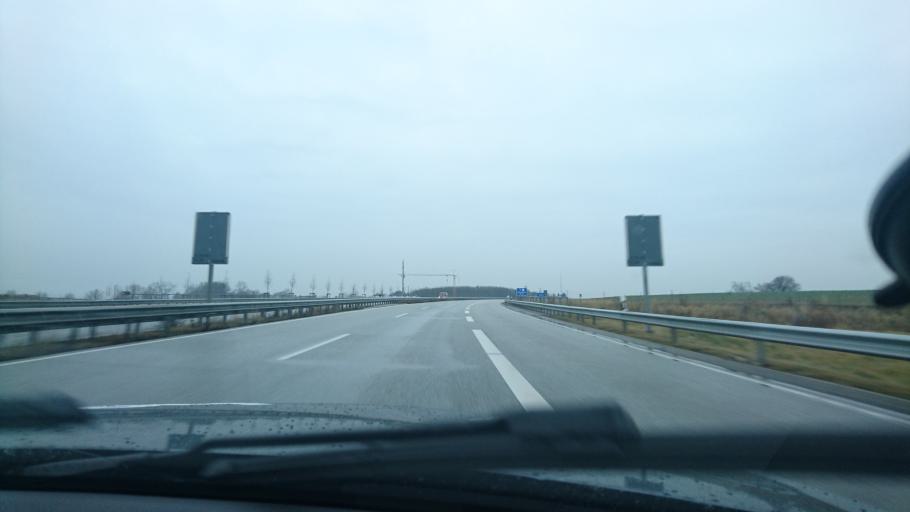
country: DE
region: Schleswig-Holstein
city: Heiligenhafen
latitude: 54.3606
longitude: 10.9630
